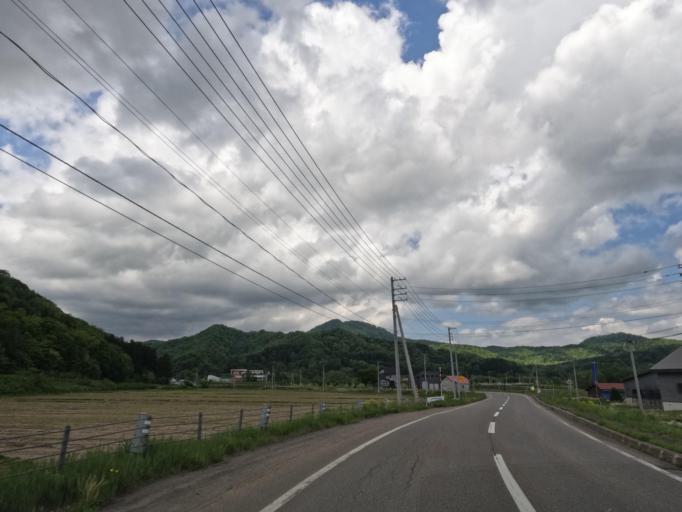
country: JP
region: Hokkaido
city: Takikawa
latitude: 43.5877
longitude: 141.7319
